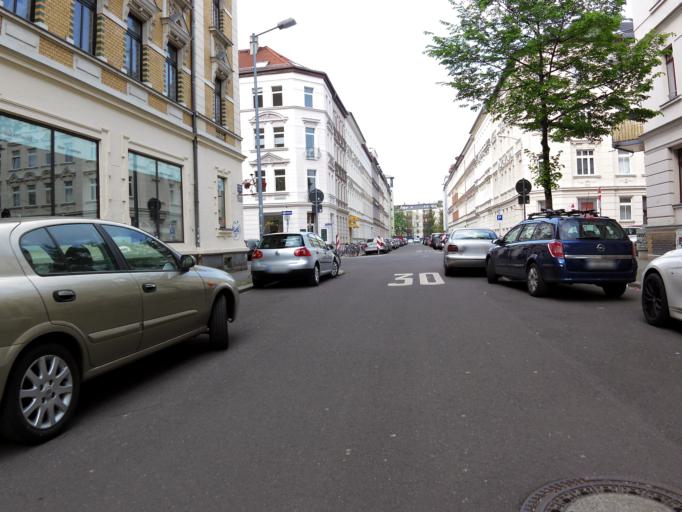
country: DE
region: Saxony
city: Leipzig
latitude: 51.3216
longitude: 12.3412
